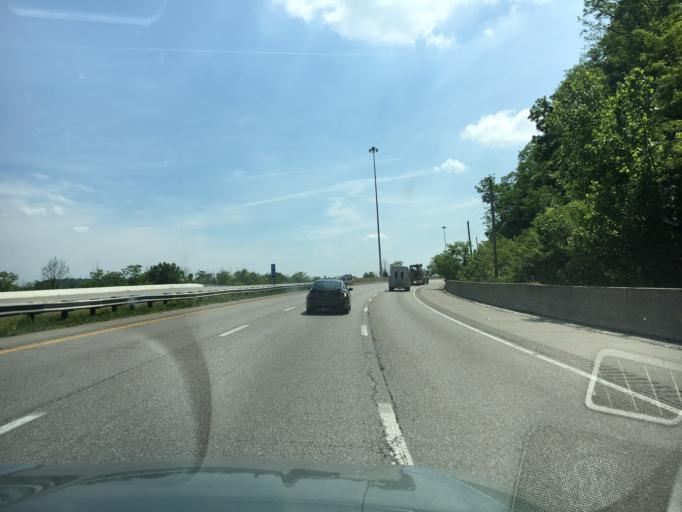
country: US
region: Ohio
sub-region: Hamilton County
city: Monfort Heights
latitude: 39.1617
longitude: -84.5582
